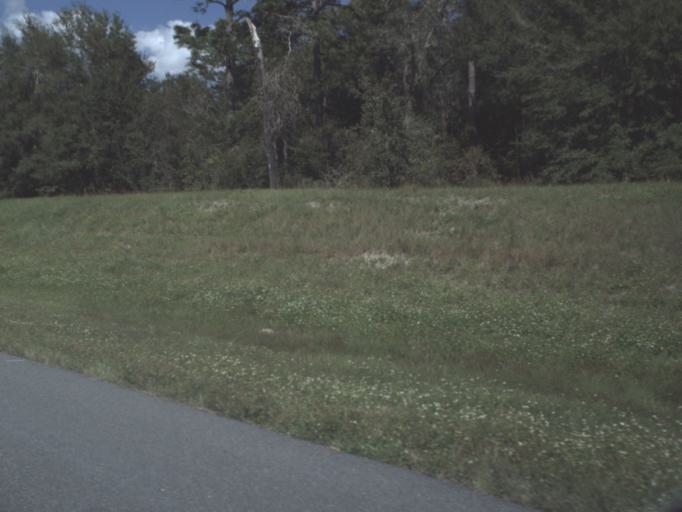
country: US
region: Florida
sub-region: Hernando County
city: Brookridge
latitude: 28.5939
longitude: -82.4858
